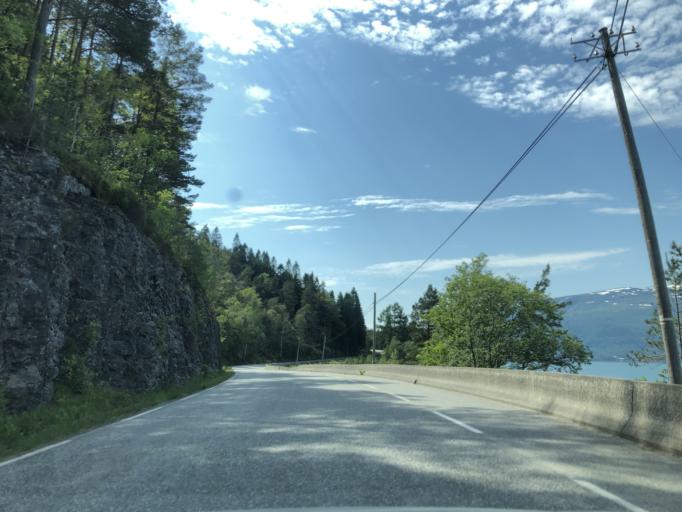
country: NO
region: Hordaland
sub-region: Jondal
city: Jondal
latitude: 60.3026
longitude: 6.2507
